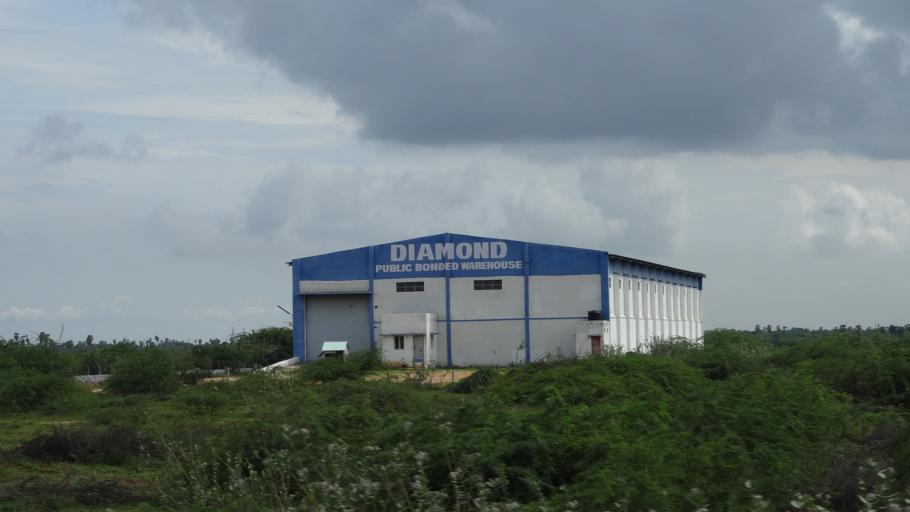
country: IN
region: Tamil Nadu
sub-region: Thoothukkudi
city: Korampallam
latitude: 8.7574
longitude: 78.0692
